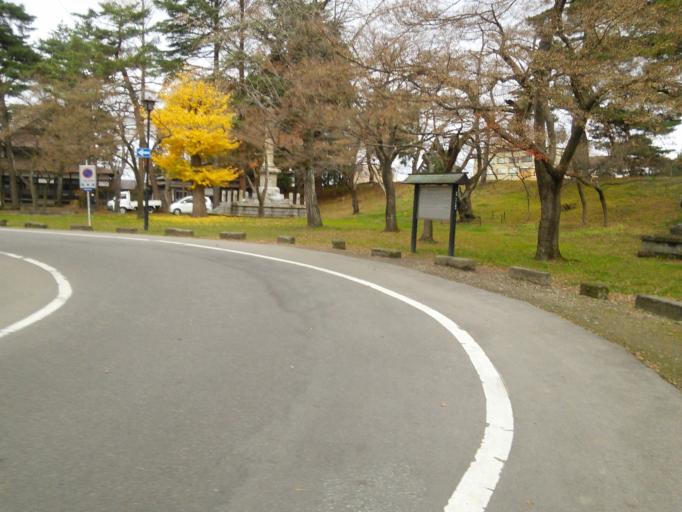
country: JP
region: Fukushima
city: Kitakata
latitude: 37.4892
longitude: 139.9305
